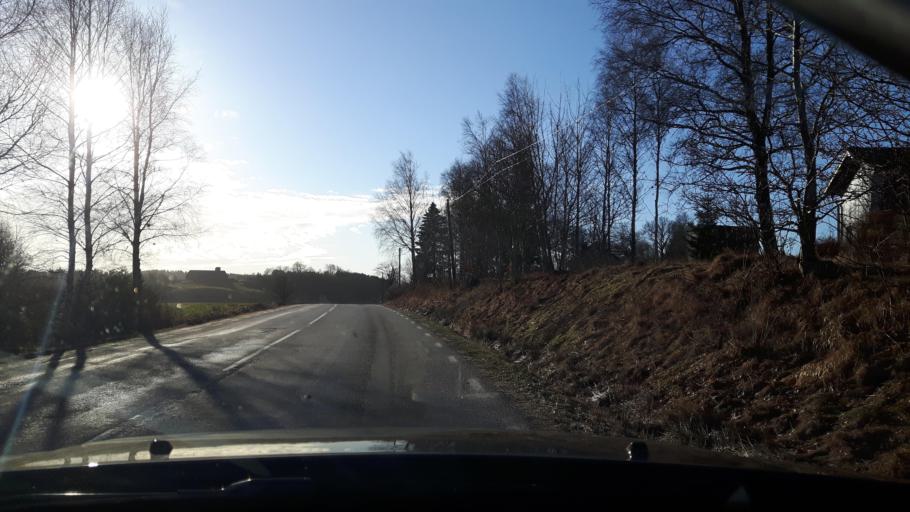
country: SE
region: Vaestra Goetaland
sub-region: Munkedals Kommun
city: Munkedal
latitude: 58.6289
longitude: 11.7734
